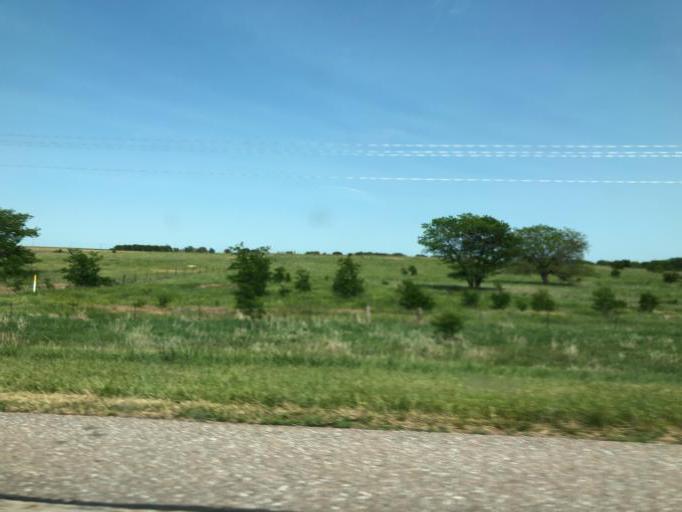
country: US
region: Nebraska
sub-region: Fillmore County
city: Geneva
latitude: 40.4042
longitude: -97.5772
